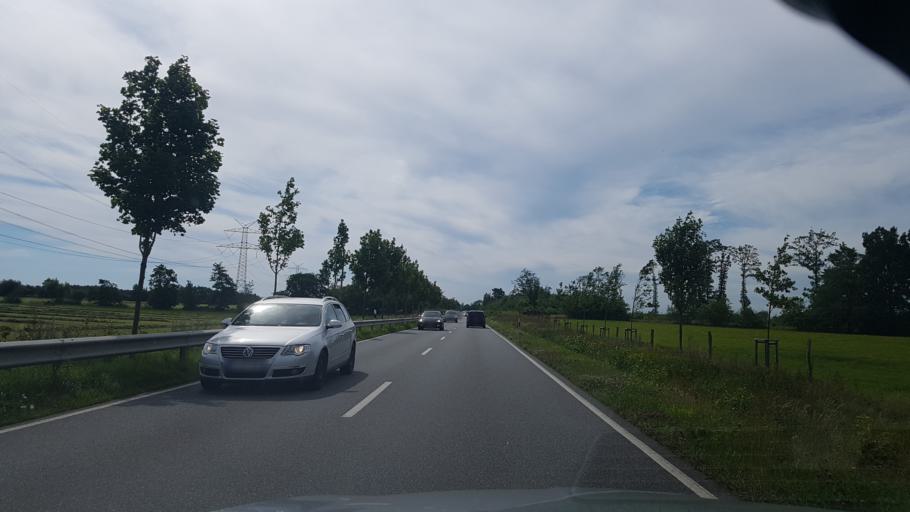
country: DE
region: Schleswig-Holstein
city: Jardelund
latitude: 54.8287
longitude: 9.2177
